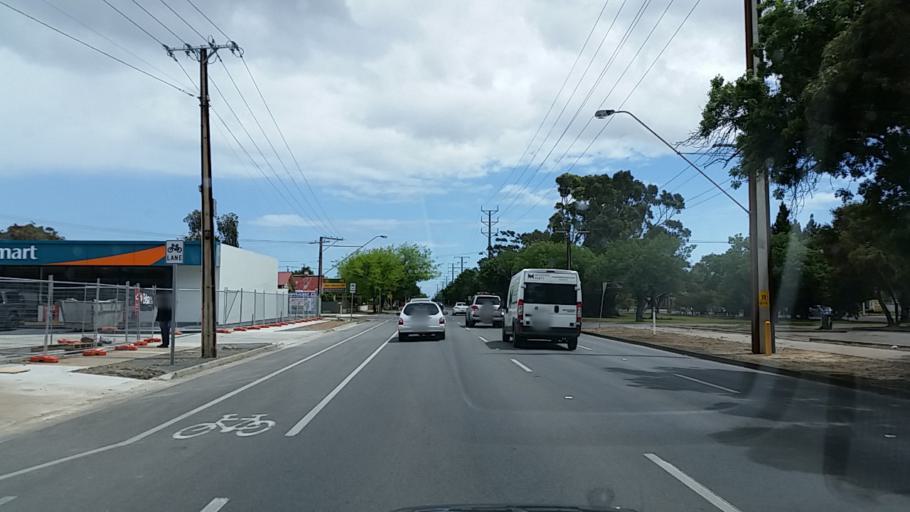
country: AU
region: South Australia
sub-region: Charles Sturt
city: Allenby Gardens
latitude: -34.8981
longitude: 138.5609
